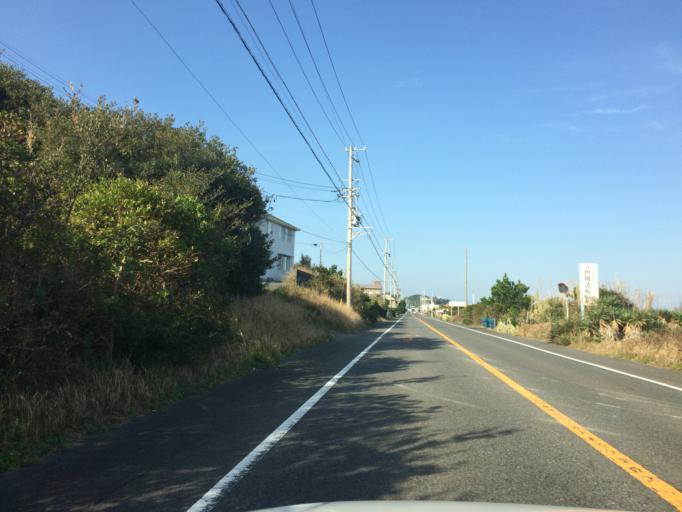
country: JP
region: Shizuoka
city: Sagara
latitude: 34.6579
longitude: 138.1938
